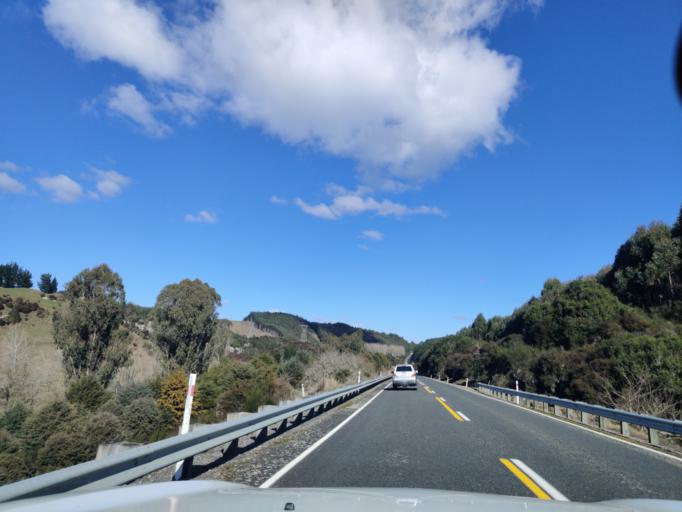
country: NZ
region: Waikato
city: Turangi
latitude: -38.6952
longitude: 175.6875
